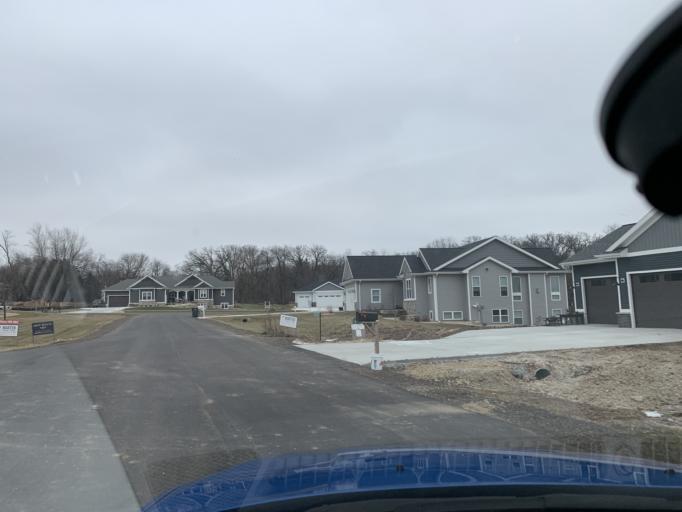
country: US
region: Wisconsin
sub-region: Dane County
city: Sun Prairie
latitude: 43.1966
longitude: -89.2654
